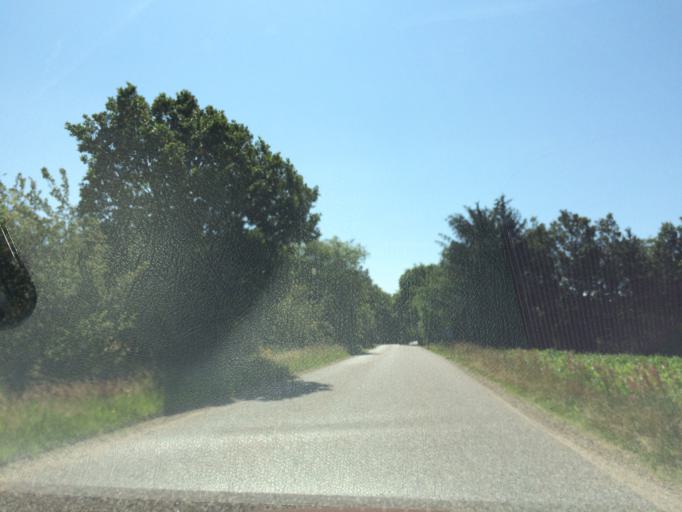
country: DK
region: Central Jutland
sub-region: Silkeborg Kommune
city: Svejbaek
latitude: 56.2367
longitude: 9.6798
